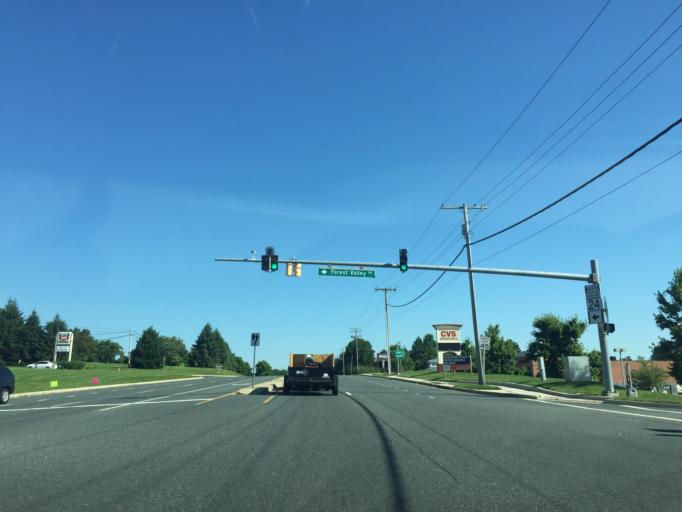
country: US
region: Maryland
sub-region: Harford County
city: Bel Air North
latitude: 39.5596
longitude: -76.3712
